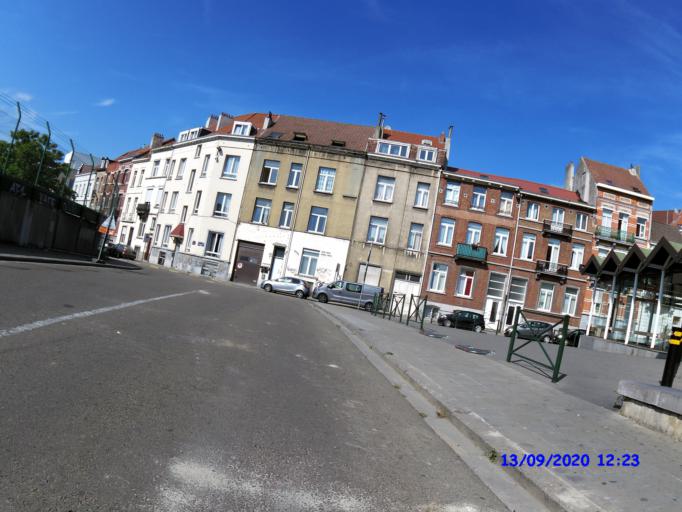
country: BE
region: Brussels Capital
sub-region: Bruxelles-Capitale
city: Brussels
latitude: 50.8626
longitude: 4.3301
